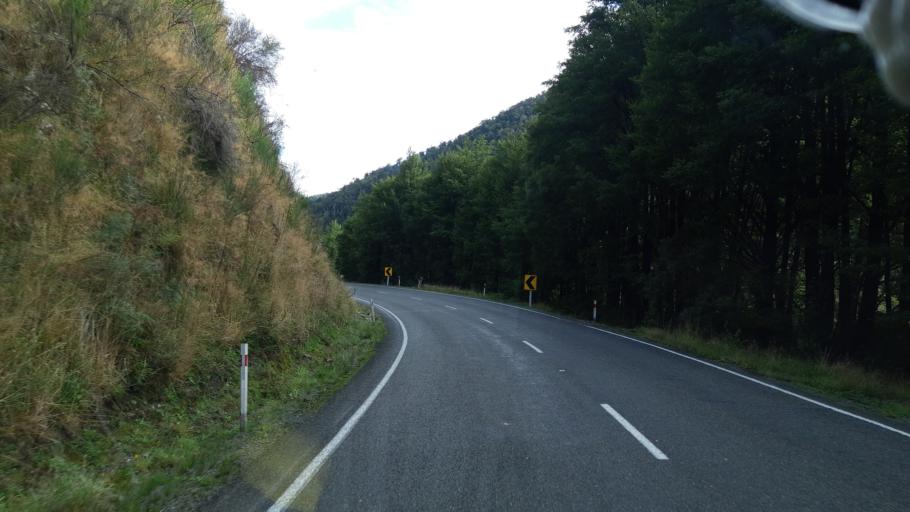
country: NZ
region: West Coast
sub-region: Buller District
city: Westport
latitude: -42.0061
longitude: 172.2330
